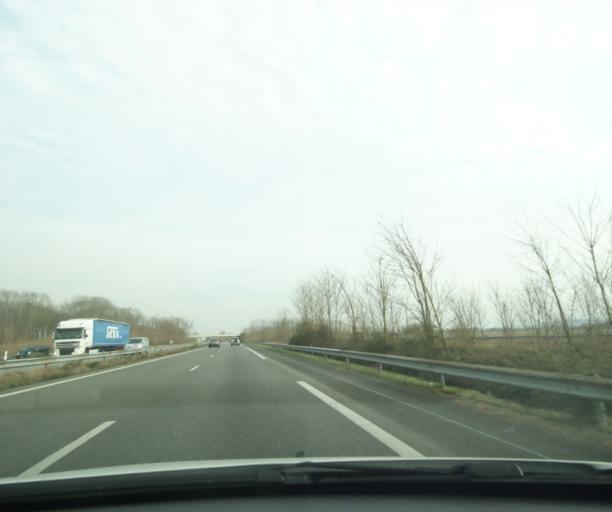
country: FR
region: Aquitaine
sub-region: Departement des Pyrenees-Atlantiques
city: Poey-de-Lescar
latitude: 43.3510
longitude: -0.4410
